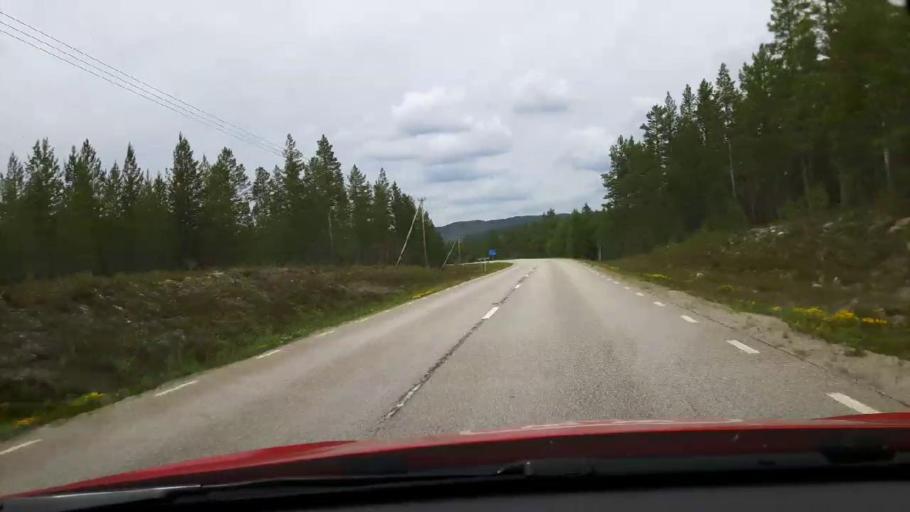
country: SE
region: Jaemtland
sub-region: Harjedalens Kommun
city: Sveg
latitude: 62.4019
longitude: 13.7406
